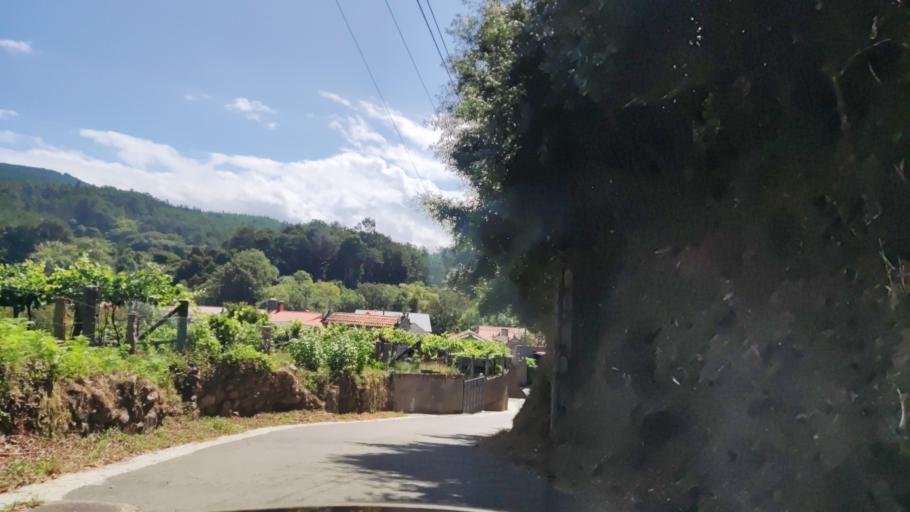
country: ES
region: Galicia
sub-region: Provincia da Coruna
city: Rianxo
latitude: 42.6980
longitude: -8.8435
